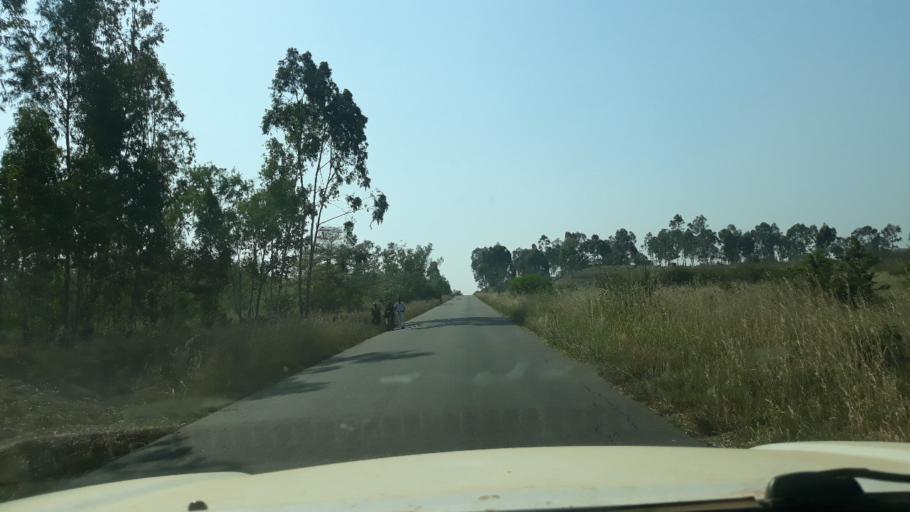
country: CD
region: South Kivu
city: Uvira
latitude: -3.1983
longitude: 29.1552
